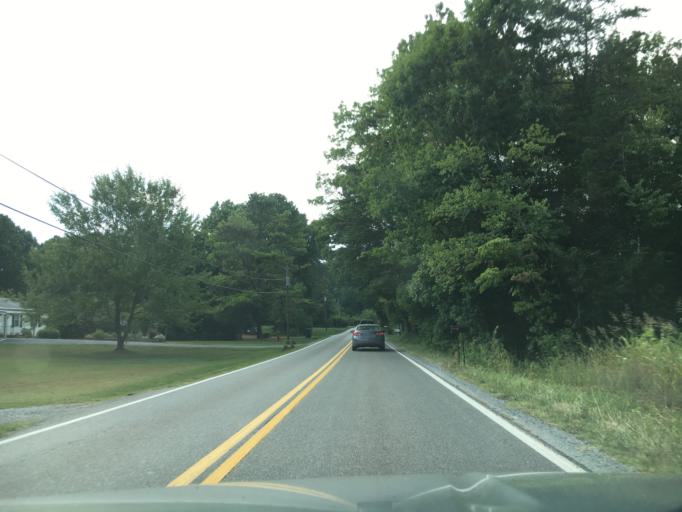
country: US
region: Virginia
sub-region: Campbell County
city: Rustburg
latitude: 37.2597
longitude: -79.1440
